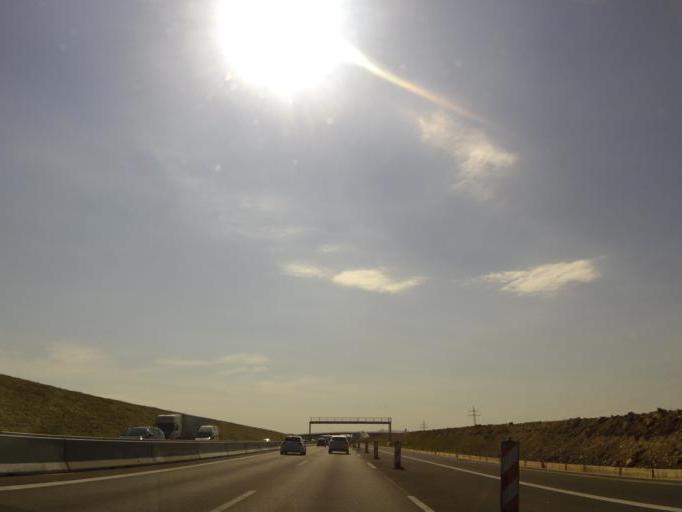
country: DE
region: Baden-Wuerttemberg
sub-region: Tuebingen Region
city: Dornstadt
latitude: 48.4655
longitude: 9.9173
